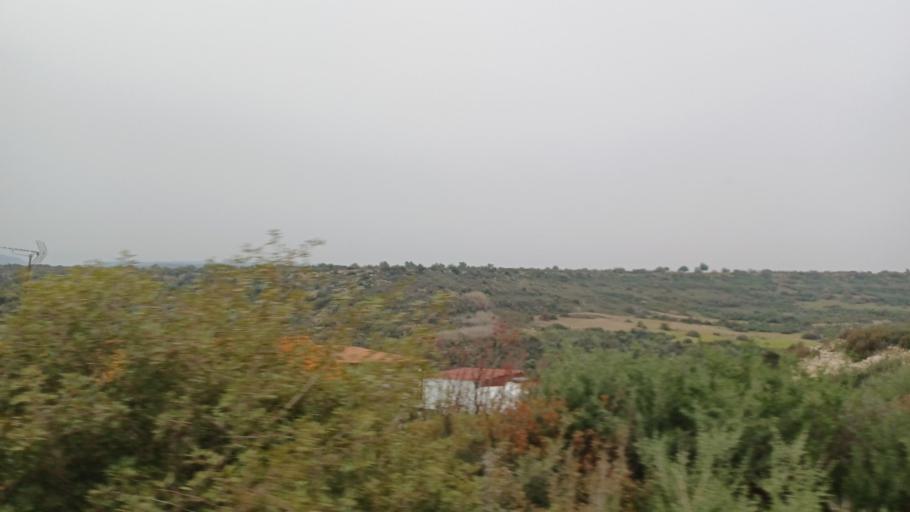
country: CY
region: Limassol
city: Pissouri
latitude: 34.7207
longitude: 32.7376
